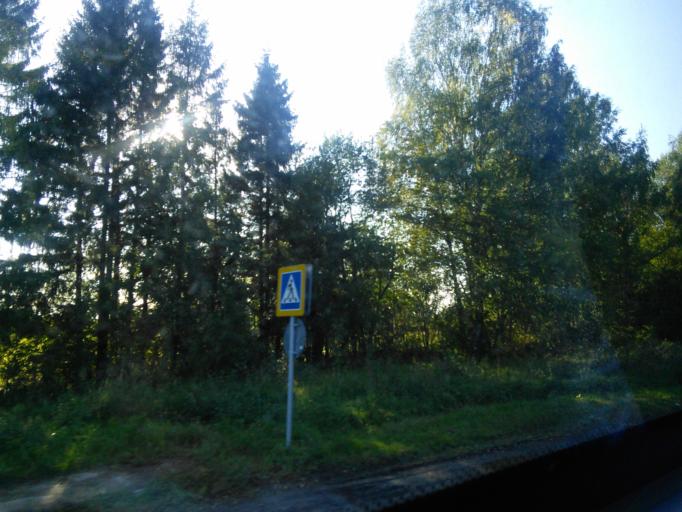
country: RU
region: Jaroslavl
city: Poshekhon'ye
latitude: 58.3652
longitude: 39.0286
